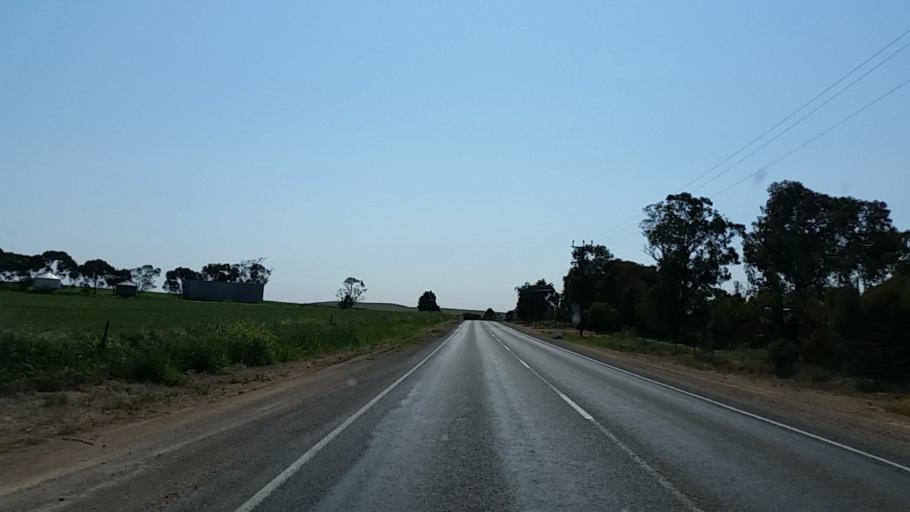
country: AU
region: South Australia
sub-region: Port Pirie City and Dists
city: Crystal Brook
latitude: -33.2569
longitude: 138.3591
